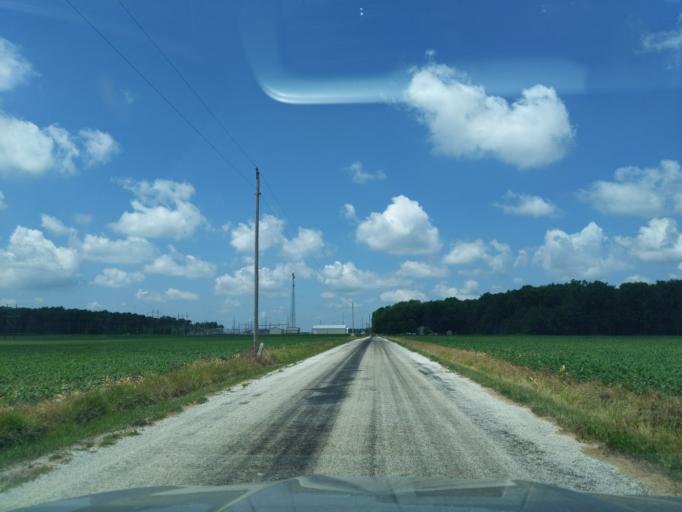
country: US
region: Indiana
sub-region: Ripley County
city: Osgood
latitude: 39.2191
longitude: -85.3380
